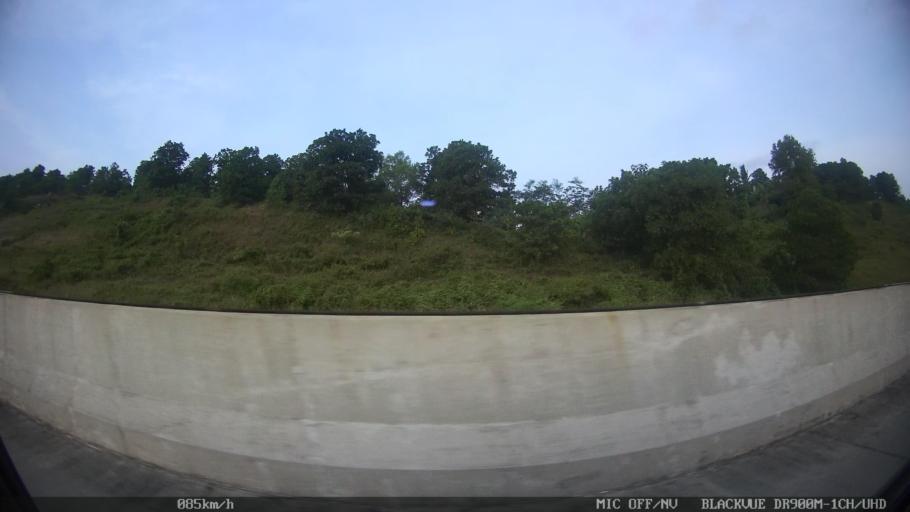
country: ID
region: Lampung
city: Penengahan
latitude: -5.8543
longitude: 105.7290
